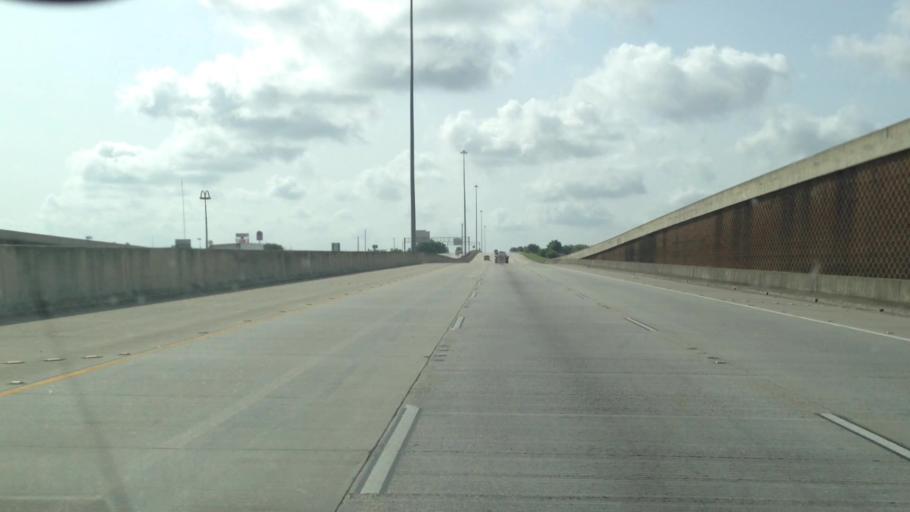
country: US
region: Louisiana
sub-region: East Baton Rouge Parish
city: Inniswold
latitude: 30.3858
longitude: -91.0715
